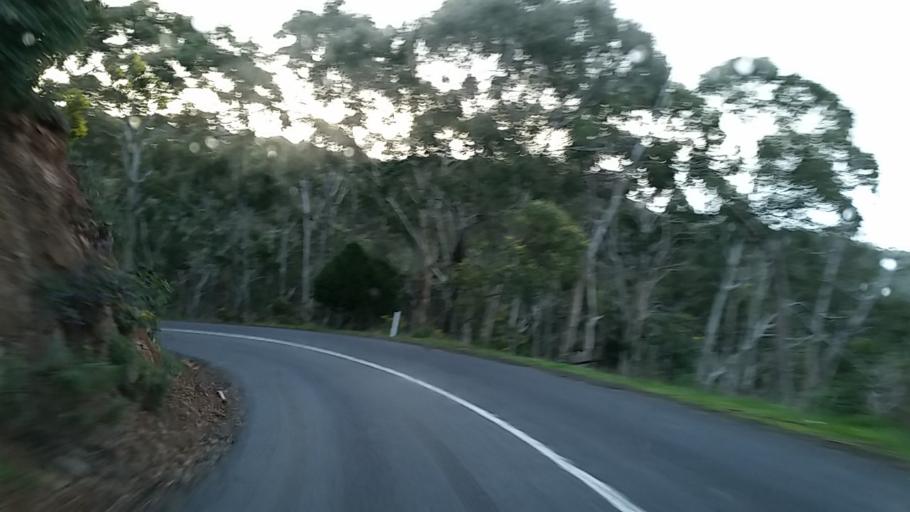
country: AU
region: South Australia
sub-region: Adelaide Hills
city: Lobethal
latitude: -34.8888
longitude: 138.8390
